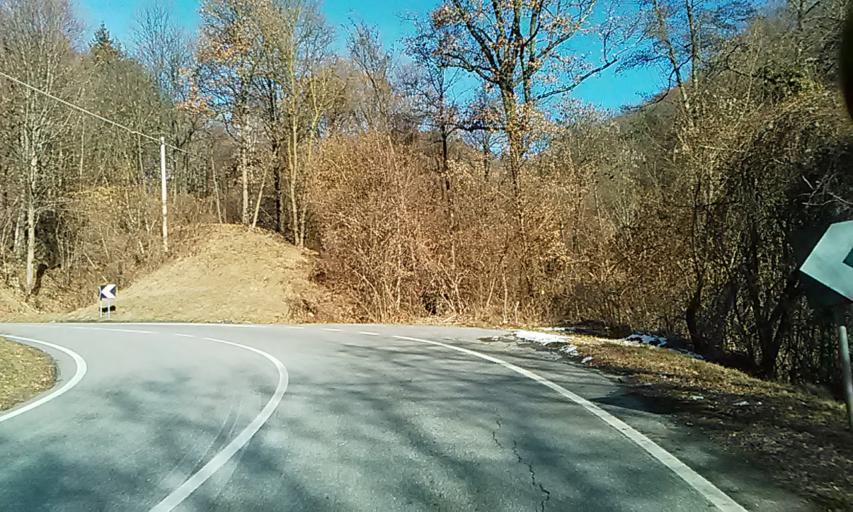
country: IT
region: Piedmont
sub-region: Provincia di Vercelli
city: Cellio
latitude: 45.7446
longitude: 8.3096
